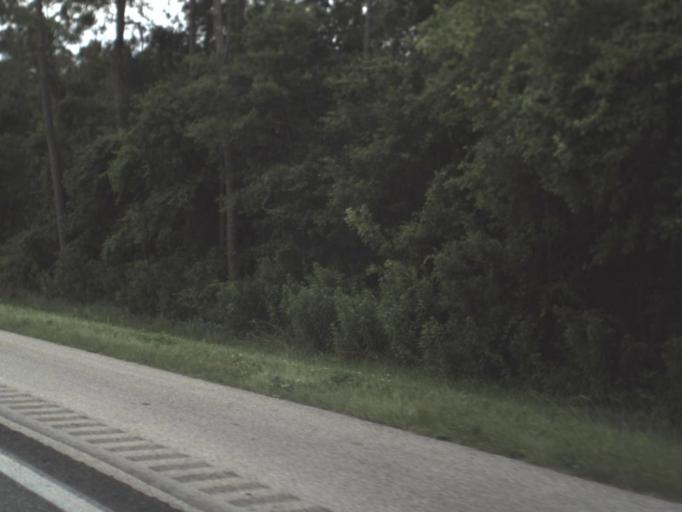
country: US
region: Florida
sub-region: Alachua County
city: Gainesville
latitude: 29.5392
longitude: -82.3282
